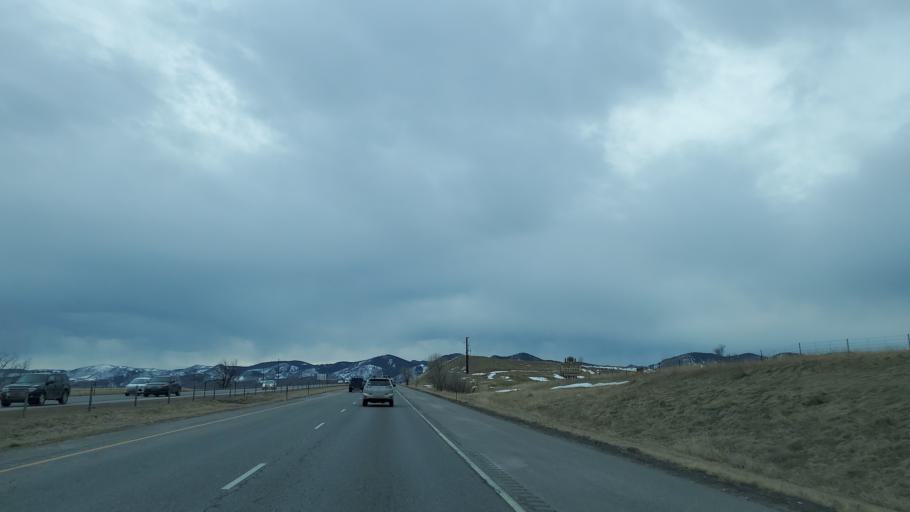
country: US
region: Colorado
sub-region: Jefferson County
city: Lakewood
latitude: 39.6508
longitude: -105.1221
